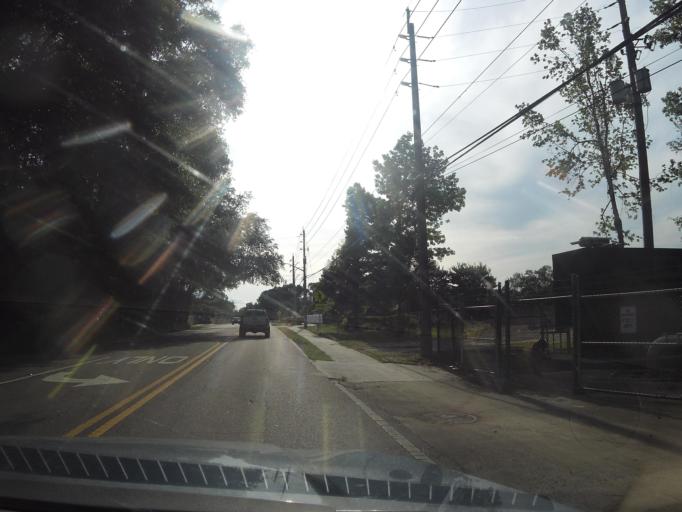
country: US
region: Florida
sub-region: Duval County
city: Jacksonville
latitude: 30.4629
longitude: -81.5678
